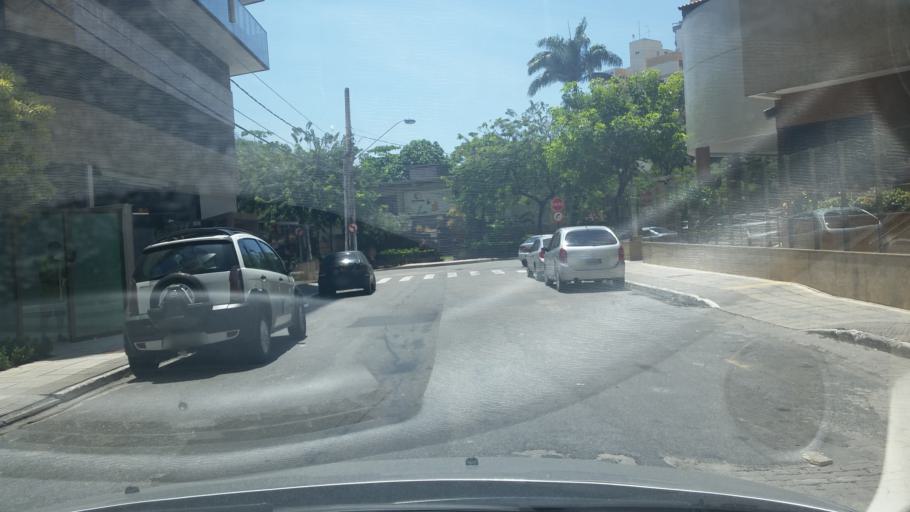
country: BR
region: Espirito Santo
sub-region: Vila Velha
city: Vila Velha
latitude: -20.3341
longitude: -40.2827
